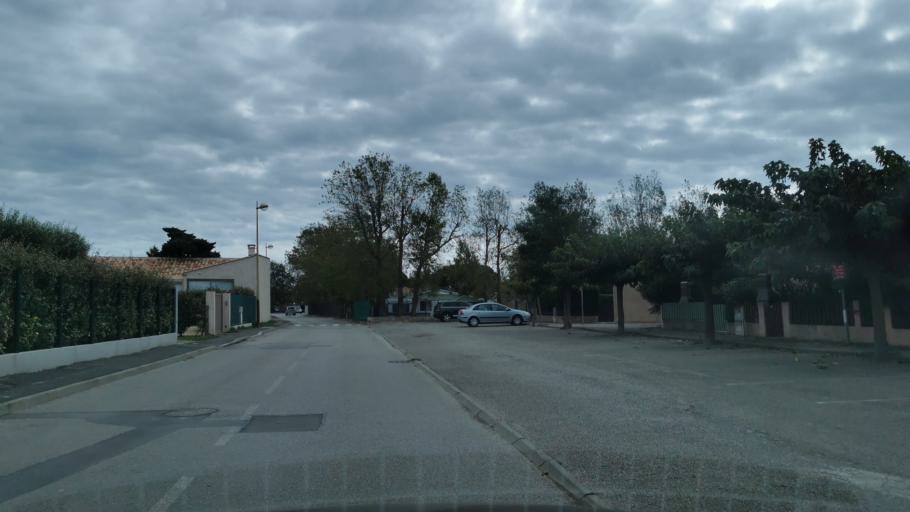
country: FR
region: Languedoc-Roussillon
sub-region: Departement de l'Herault
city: Vendres
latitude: 43.2163
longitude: 3.2298
